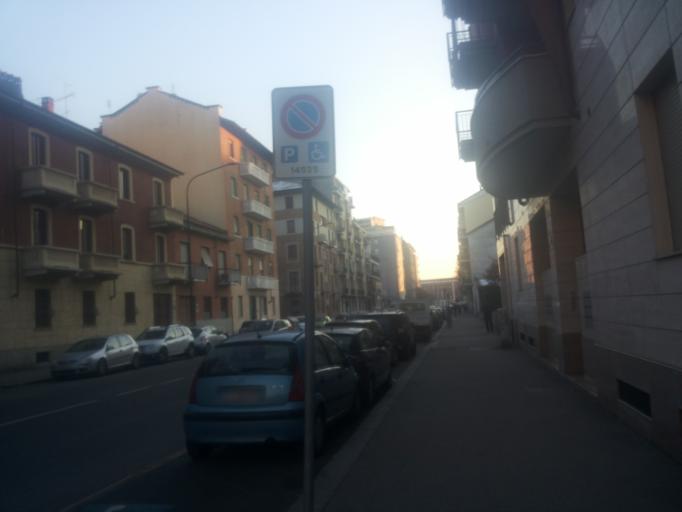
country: IT
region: Piedmont
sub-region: Provincia di Torino
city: Lesna
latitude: 45.0595
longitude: 7.6449
